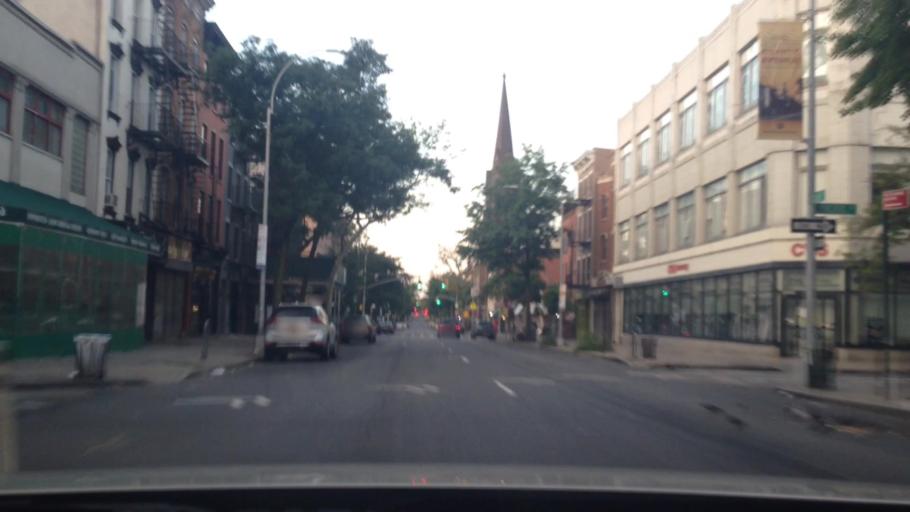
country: US
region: New York
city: New York City
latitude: 40.6892
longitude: -73.9925
